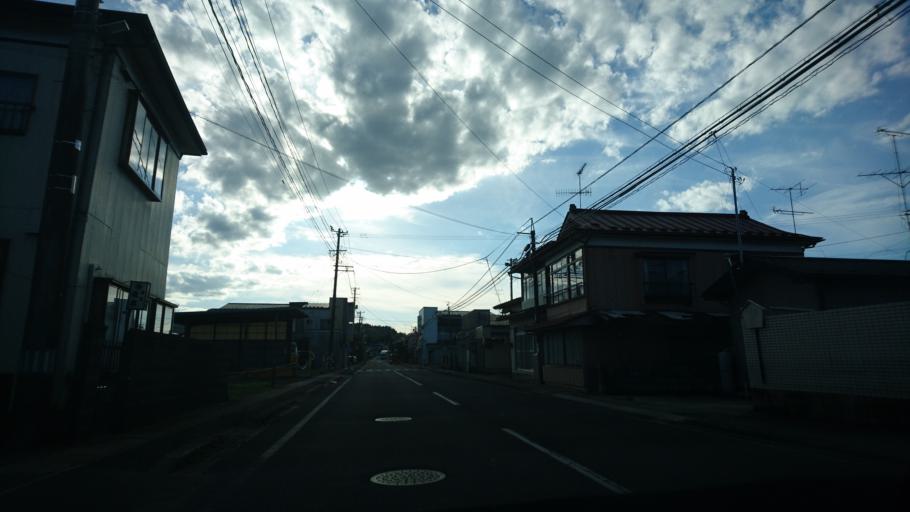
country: JP
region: Iwate
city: Ichinoseki
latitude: 38.8479
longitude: 141.1748
